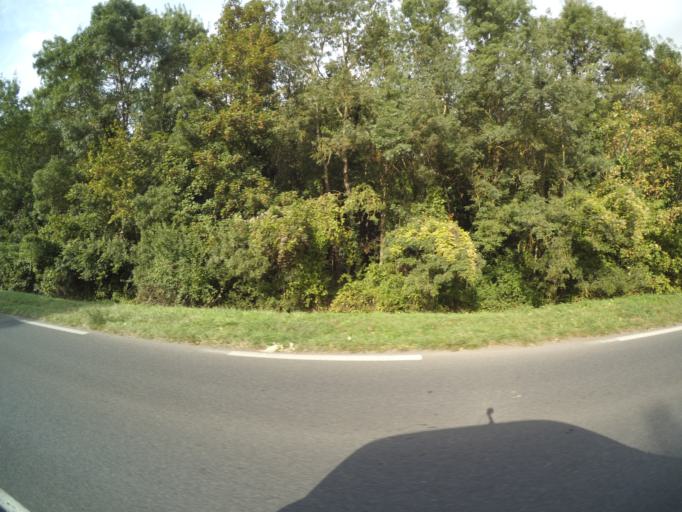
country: FR
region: Centre
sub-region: Departement d'Indre-et-Loire
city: Vouvray
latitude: 47.4102
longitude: 0.7894
